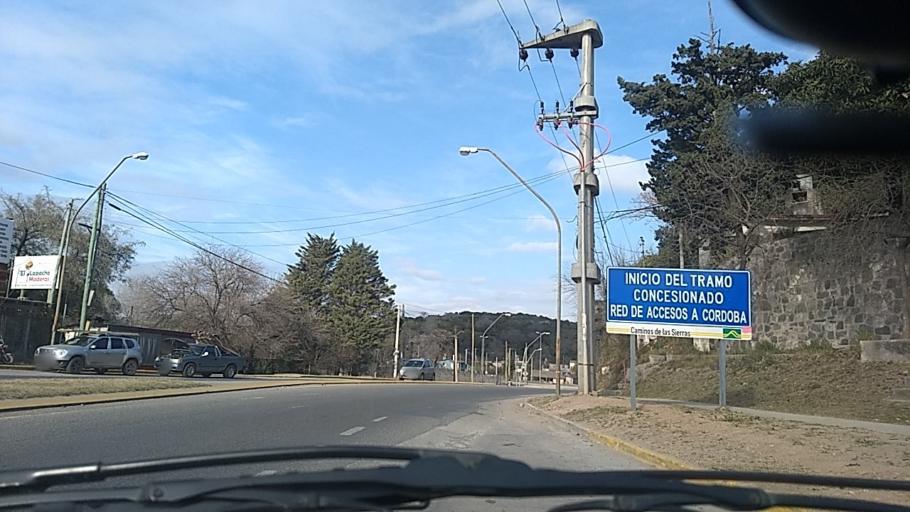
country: AR
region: Cordoba
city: Salsipuedes
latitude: -31.1426
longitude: -64.2977
